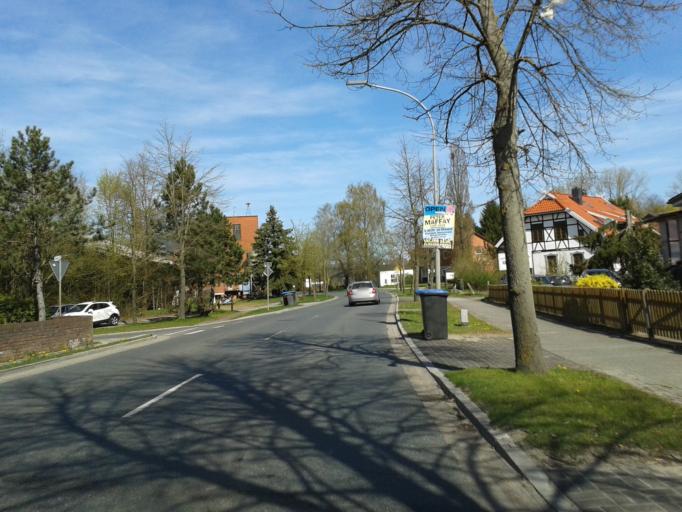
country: DE
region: Lower Saxony
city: Gerdau
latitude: 52.9638
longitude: 10.4163
